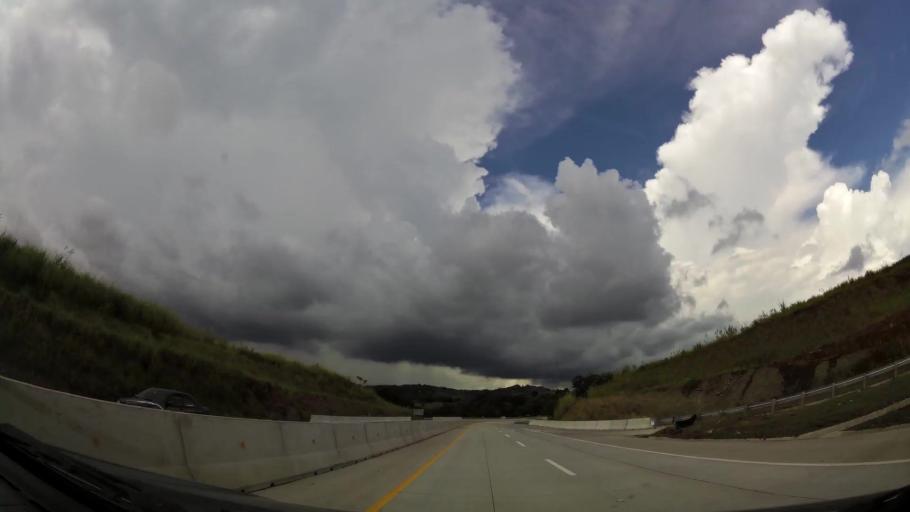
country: PA
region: Panama
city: San Miguelito
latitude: 9.0878
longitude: -79.4424
